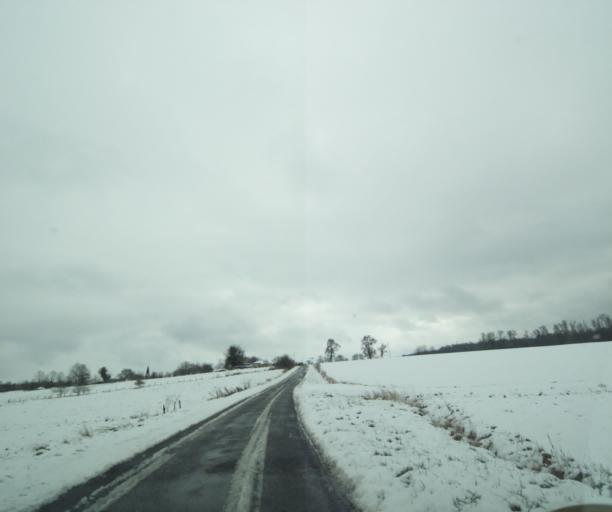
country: FR
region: Champagne-Ardenne
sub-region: Departement de la Haute-Marne
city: Montier-en-Der
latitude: 48.4161
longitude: 4.7346
